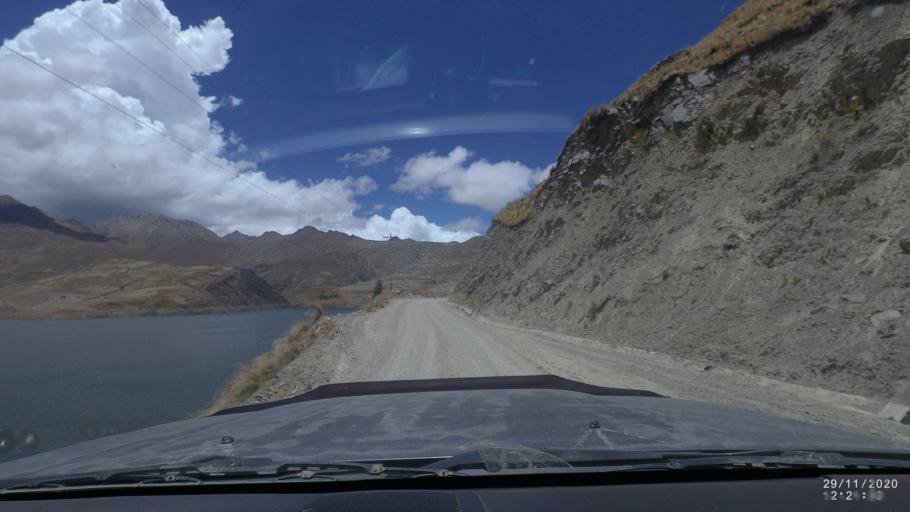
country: BO
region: Cochabamba
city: Cochabamba
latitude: -17.0986
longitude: -66.3234
